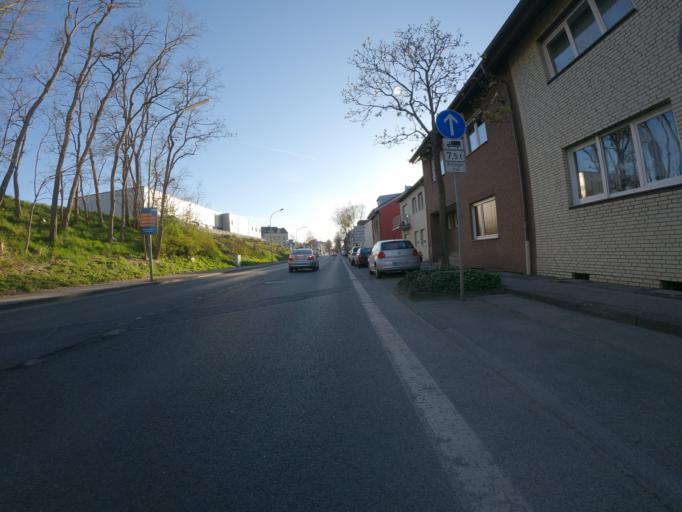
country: DE
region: North Rhine-Westphalia
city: Stolberg
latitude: 50.7746
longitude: 6.2127
